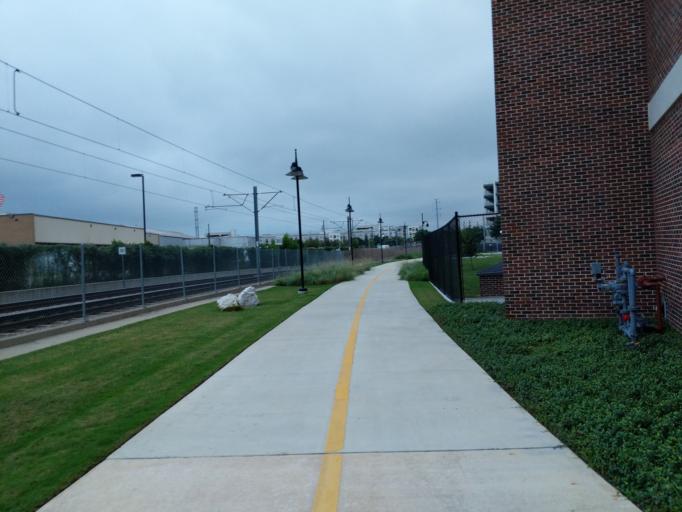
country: US
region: Texas
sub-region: Dallas County
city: Highland Park
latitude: 32.8418
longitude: -96.7728
